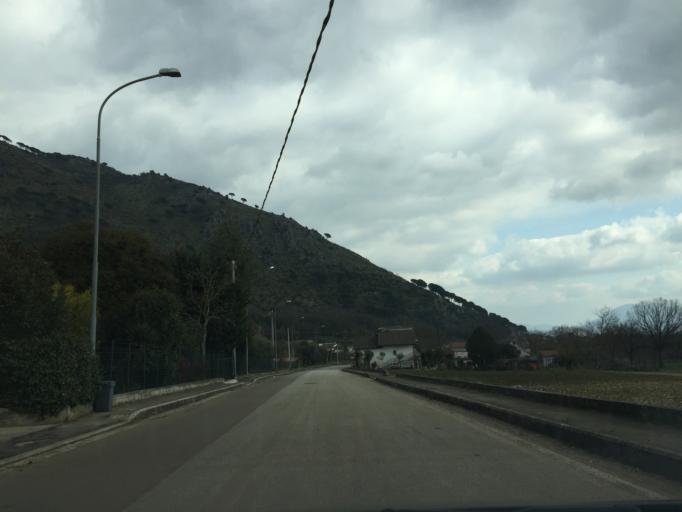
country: IT
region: Latium
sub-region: Provincia di Frosinone
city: Villa Santa Lucia
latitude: 41.4943
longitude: 13.7761
